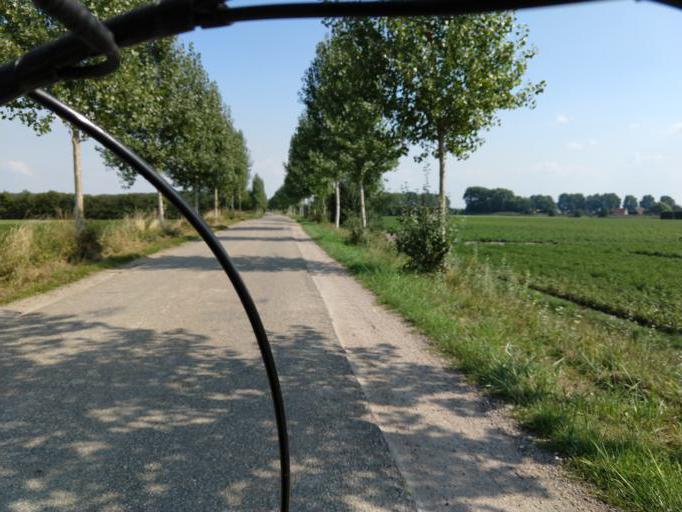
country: NL
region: Zeeland
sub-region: Gemeente Goes
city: Goes
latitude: 51.4410
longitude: 3.8699
